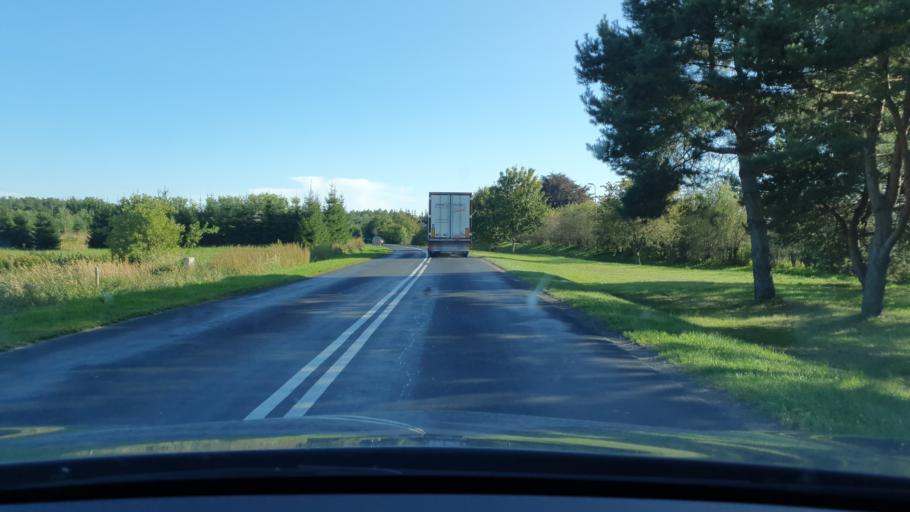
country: PL
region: West Pomeranian Voivodeship
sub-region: Powiat kamienski
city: Golczewo
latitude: 53.8219
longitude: 14.9882
